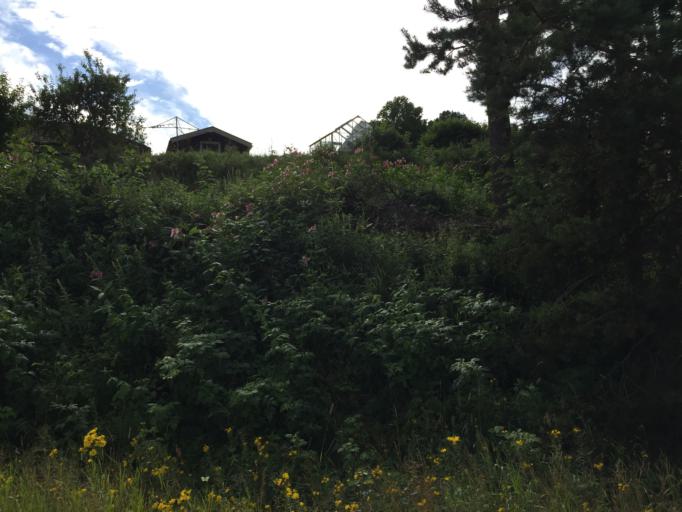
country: SE
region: Gaevleborg
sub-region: Ljusdals Kommun
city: Jaervsoe
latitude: 61.7172
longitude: 16.1815
